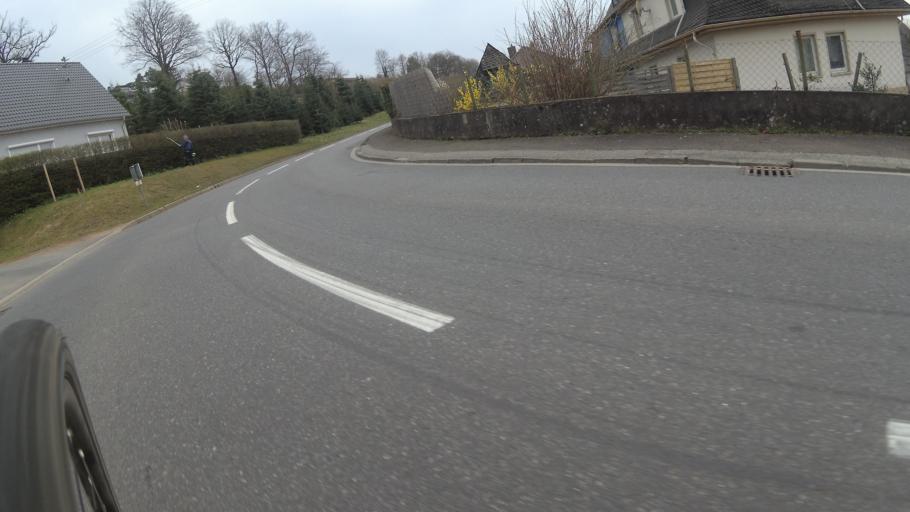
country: DE
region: Rheinland-Pfalz
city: Birkenfeld
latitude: 49.6448
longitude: 7.1733
